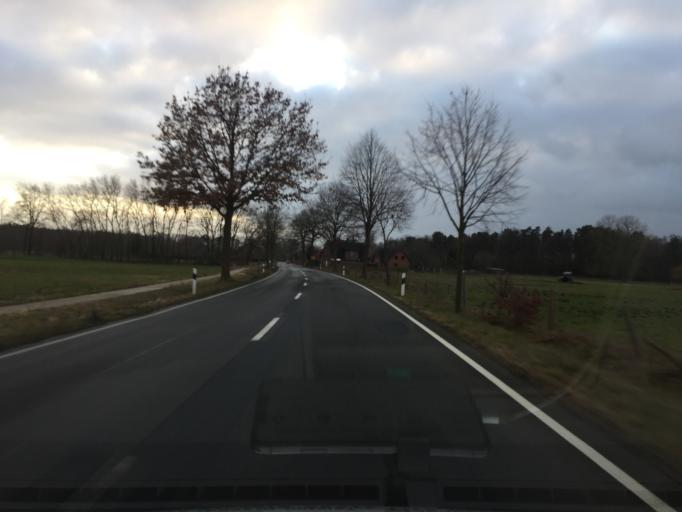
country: DE
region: Lower Saxony
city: Garbsen
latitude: 52.4367
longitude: 9.5208
